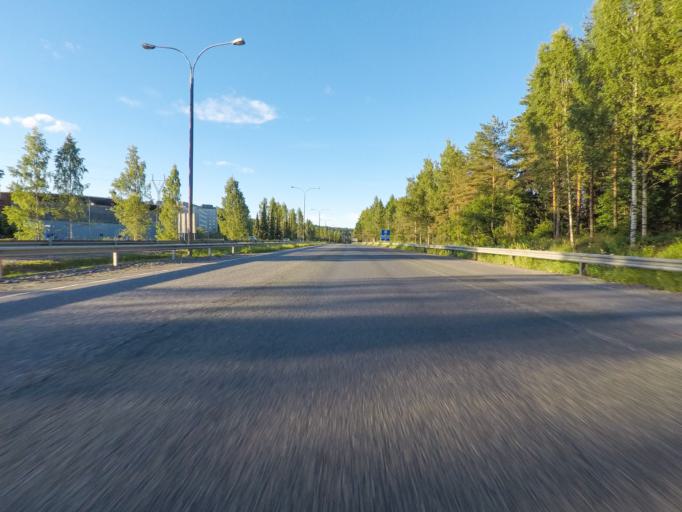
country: FI
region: Northern Savo
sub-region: Kuopio
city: Kuopio
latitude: 62.8939
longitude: 27.6470
